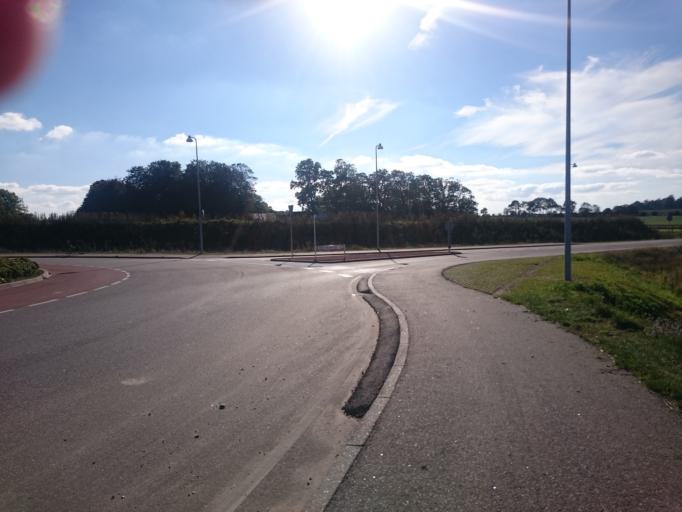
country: DK
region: South Denmark
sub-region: Vejen Kommune
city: Vejen
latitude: 55.4918
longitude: 9.1031
